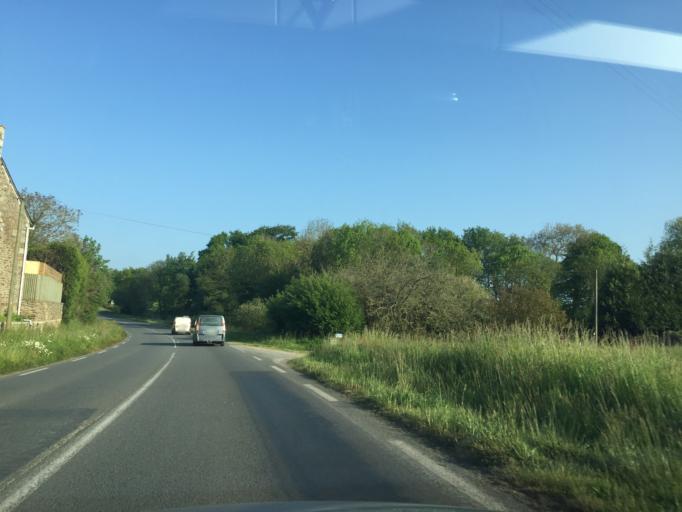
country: FR
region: Brittany
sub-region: Departement des Cotes-d'Armor
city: Saint-Cast-le-Guildo
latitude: 48.5879
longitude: -2.2430
